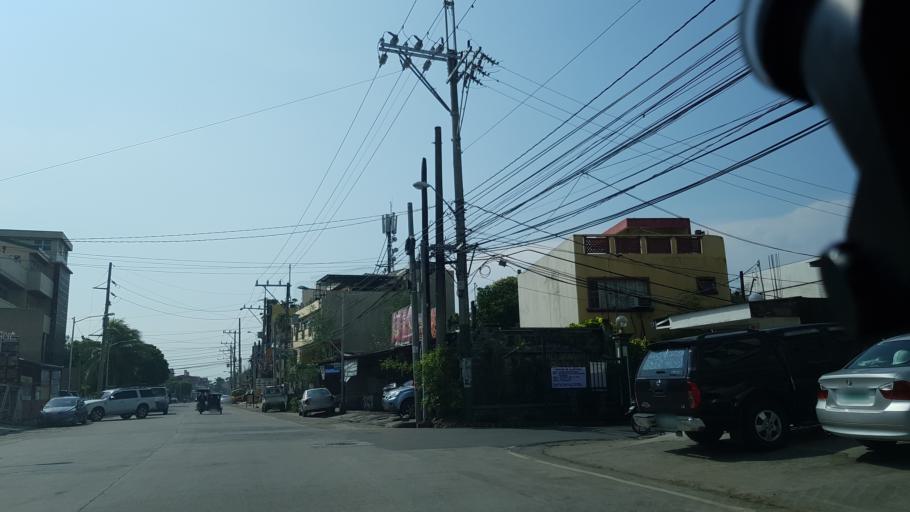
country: PH
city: Sambayanihan People's Village
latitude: 14.4879
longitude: 121.0236
